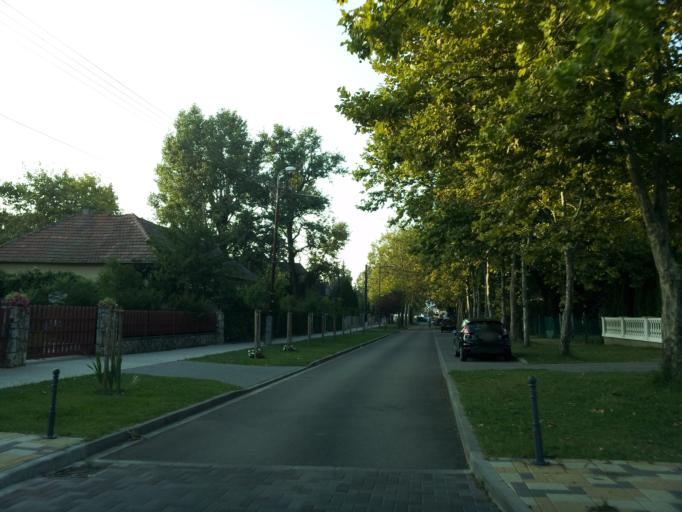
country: HU
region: Somogy
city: Zamardi
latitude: 46.8834
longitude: 17.9431
